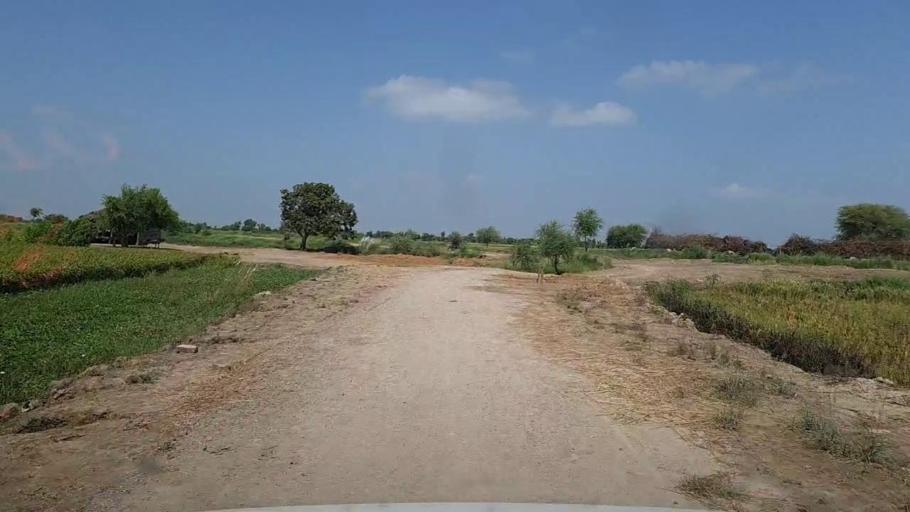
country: PK
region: Sindh
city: Kario
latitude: 24.6866
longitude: 68.6015
